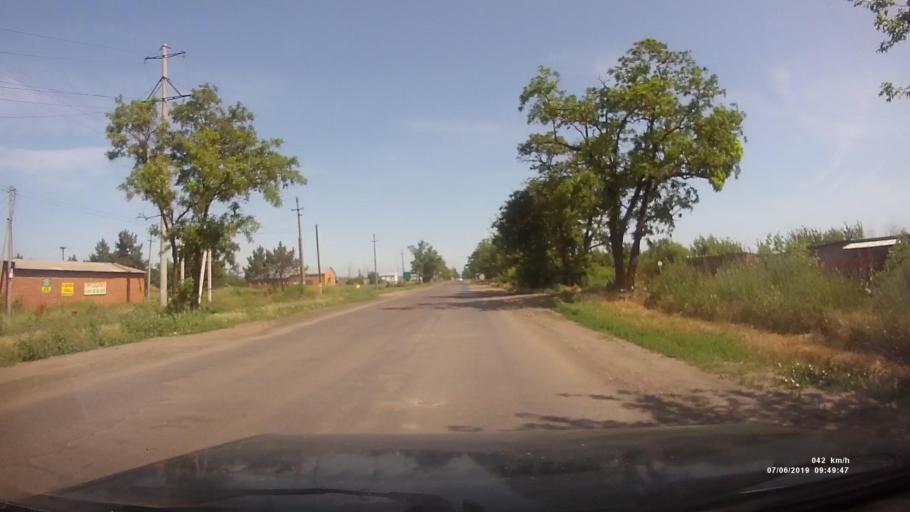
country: RU
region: Rostov
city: Azov
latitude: 47.0739
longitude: 39.4378
